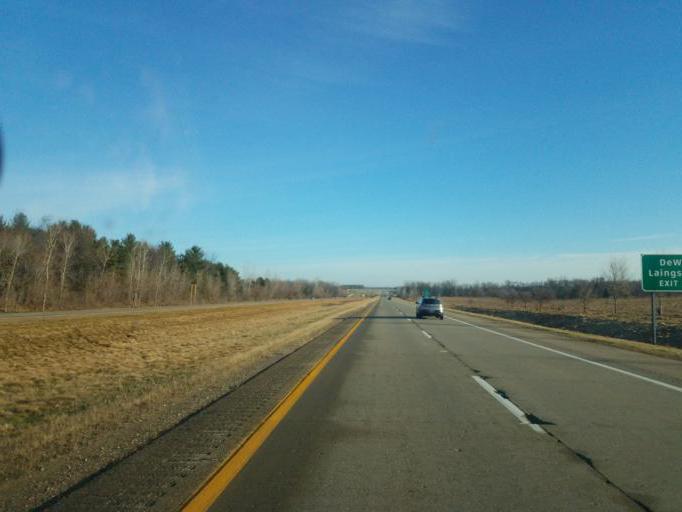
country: US
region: Michigan
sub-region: Clinton County
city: DeWitt
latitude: 42.8477
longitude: -84.5186
